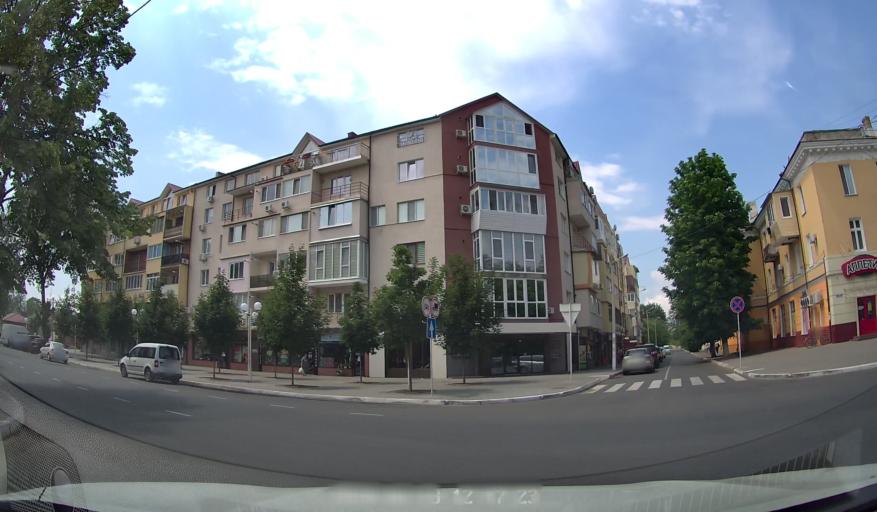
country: GR
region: Attica
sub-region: Nomos Piraios
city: Kythira
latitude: 36.2770
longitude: 23.0657
